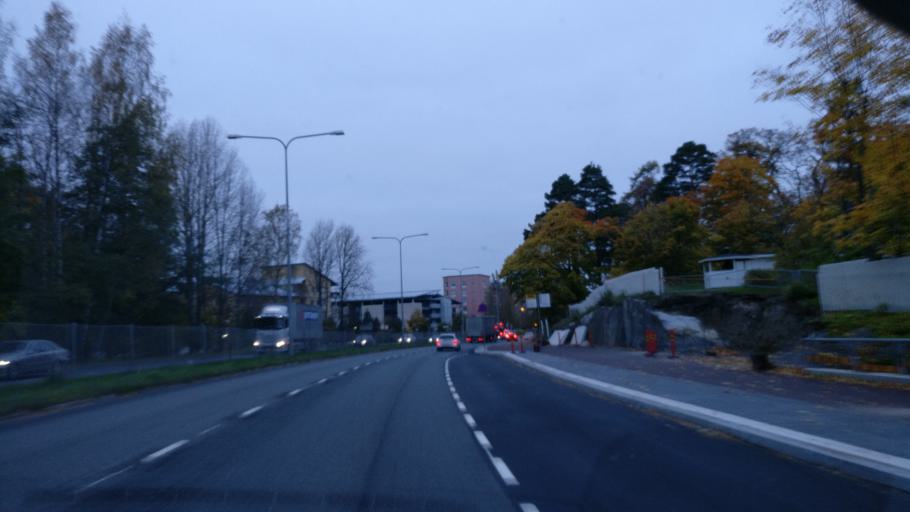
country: FI
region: Uusimaa
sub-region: Helsinki
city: Vantaa
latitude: 60.1870
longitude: 25.0428
